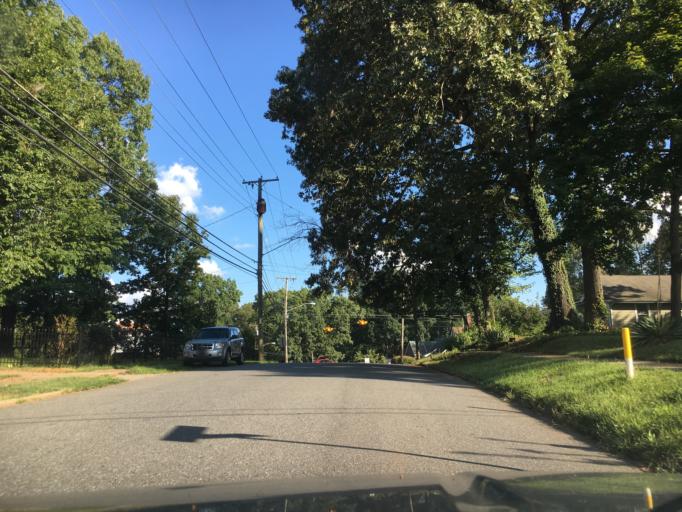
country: US
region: Virginia
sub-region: City of Lynchburg
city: West Lynchburg
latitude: 37.3867
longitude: -79.1837
